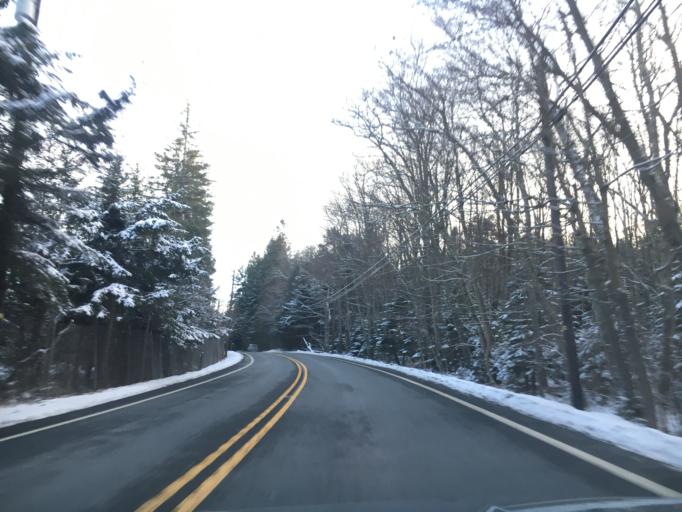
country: US
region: Pennsylvania
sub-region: Pike County
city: Hemlock Farms
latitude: 41.2494
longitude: -75.0692
